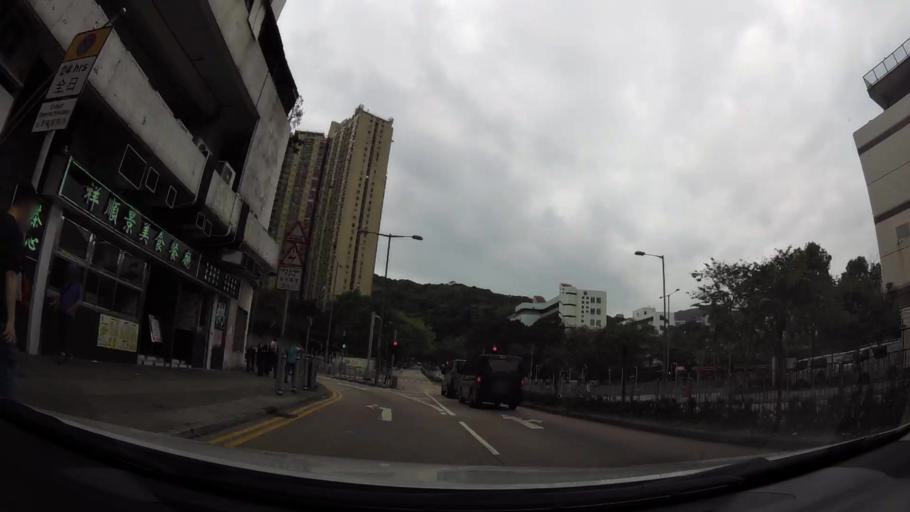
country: HK
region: Tuen Mun
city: Tuen Mun
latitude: 22.4008
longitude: 113.9682
